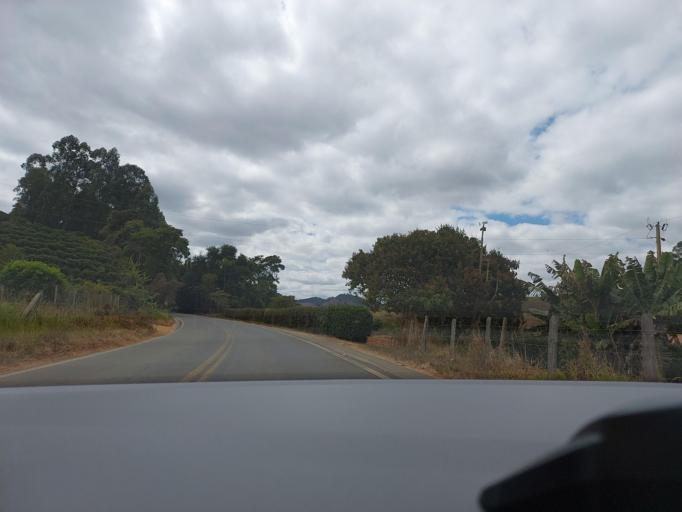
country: BR
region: Minas Gerais
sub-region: Vicosa
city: Vicosa
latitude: -20.8279
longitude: -42.7379
